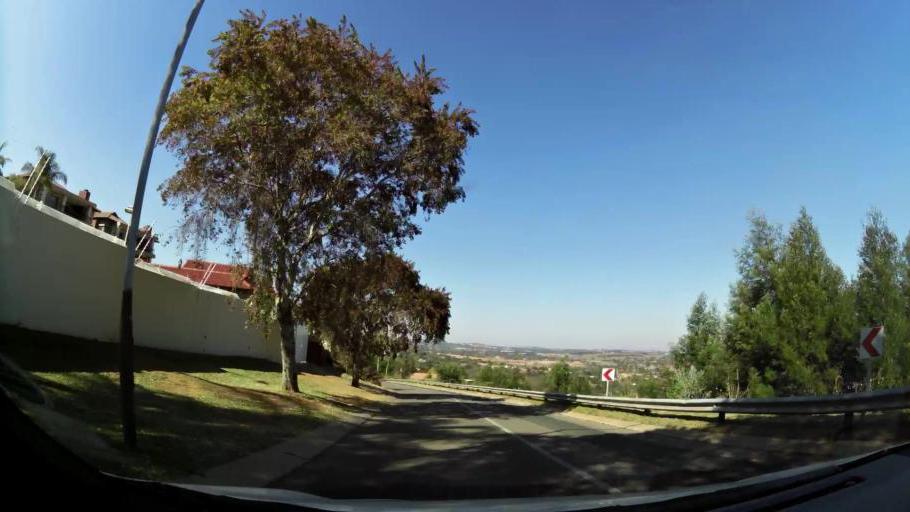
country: ZA
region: Gauteng
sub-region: City of Tshwane Metropolitan Municipality
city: Pretoria
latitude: -25.7919
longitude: 28.2308
